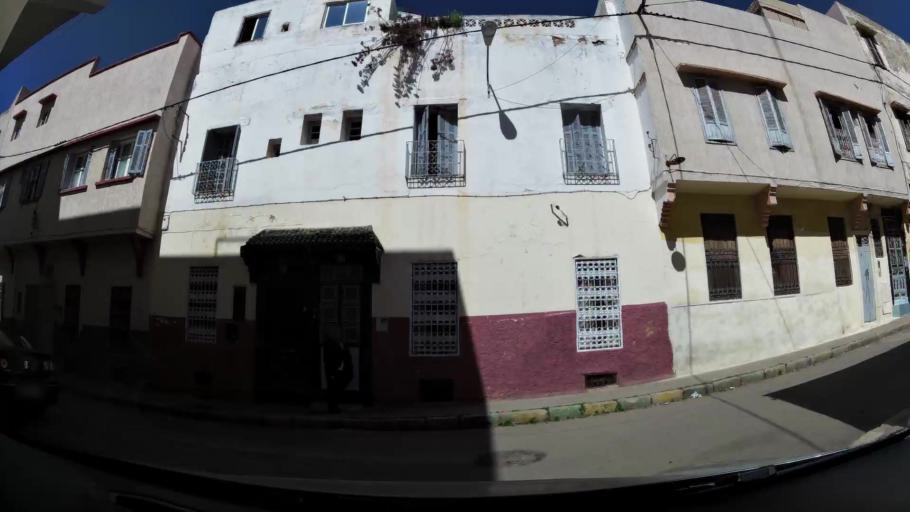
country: MA
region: Meknes-Tafilalet
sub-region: Meknes
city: Meknes
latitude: 33.8888
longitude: -5.5717
